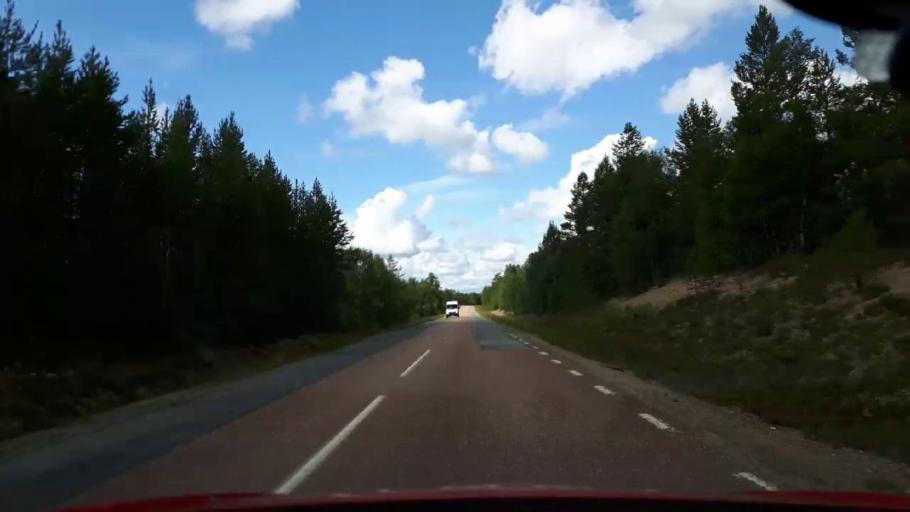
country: SE
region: Dalarna
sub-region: Alvdalens Kommun
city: AElvdalen
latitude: 61.7986
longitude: 13.6806
